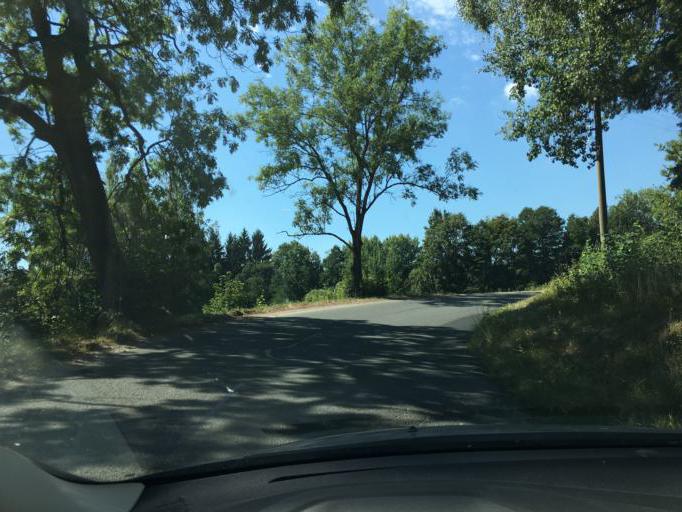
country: CZ
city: Plavy
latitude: 50.7026
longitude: 15.3525
